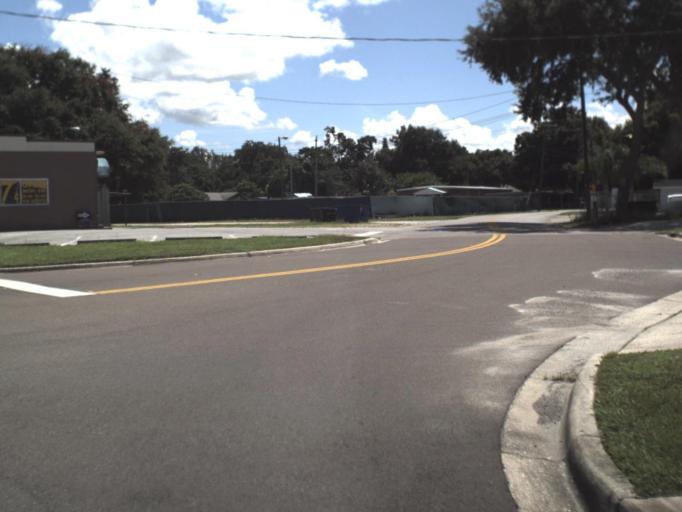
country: US
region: Florida
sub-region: Polk County
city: Inwood
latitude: 28.0473
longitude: -81.7626
